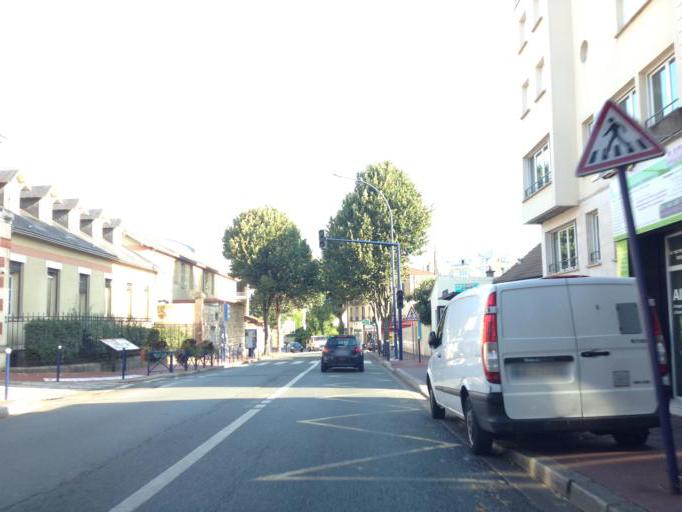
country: FR
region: Ile-de-France
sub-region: Departement des Hauts-de-Seine
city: Clamart
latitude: 48.8143
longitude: 2.2578
